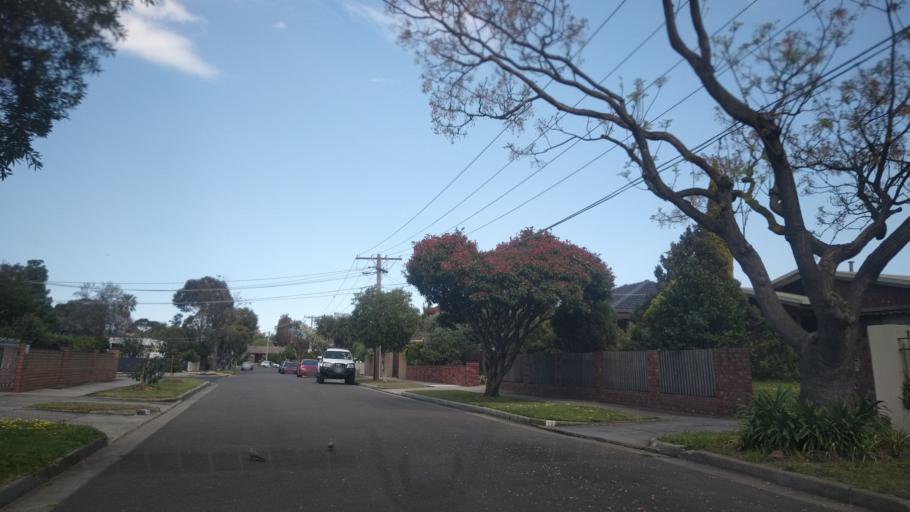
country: AU
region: Victoria
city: Highett
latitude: -37.9576
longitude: 145.0475
